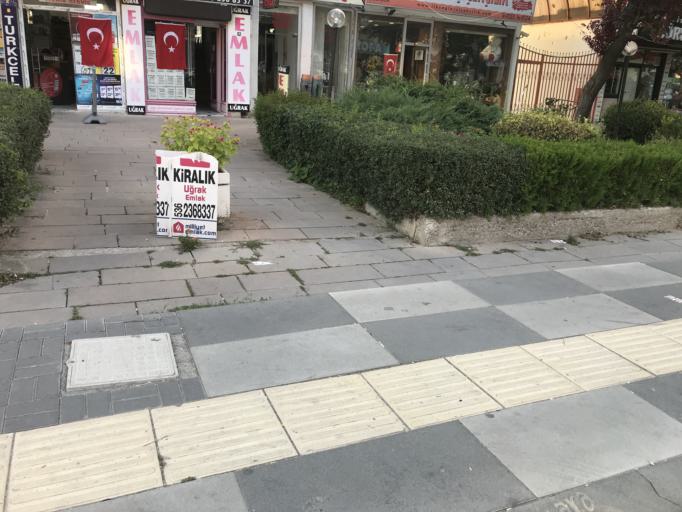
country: TR
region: Ankara
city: Ankara
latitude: 39.8706
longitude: 32.8285
